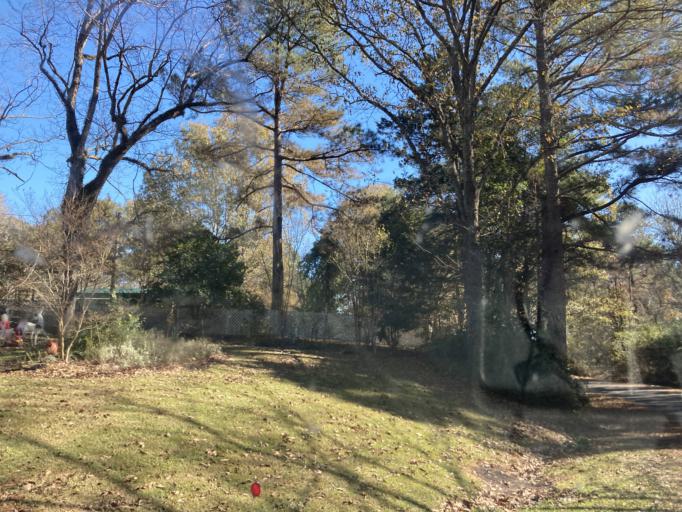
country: US
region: Mississippi
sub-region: Hinds County
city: Lynchburg
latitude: 32.5807
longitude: -90.5624
